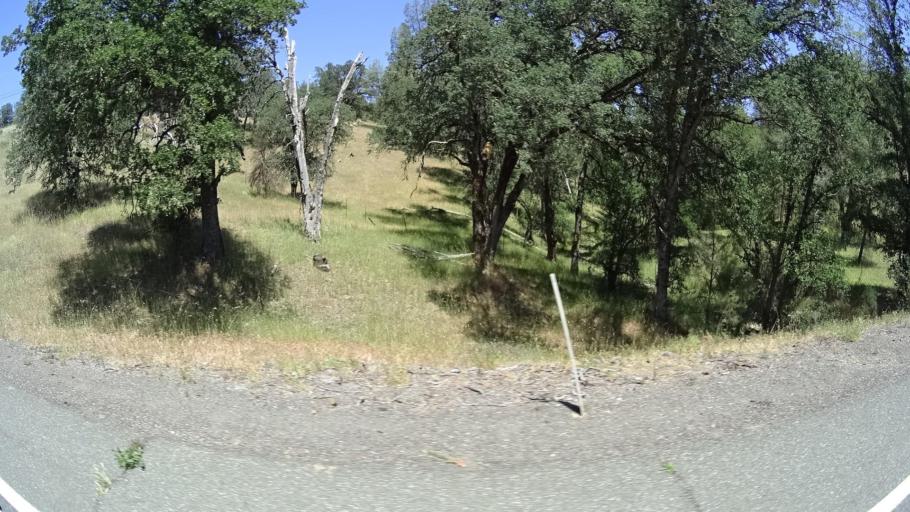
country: US
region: California
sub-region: Lake County
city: Lower Lake
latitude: 38.8558
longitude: -122.6229
